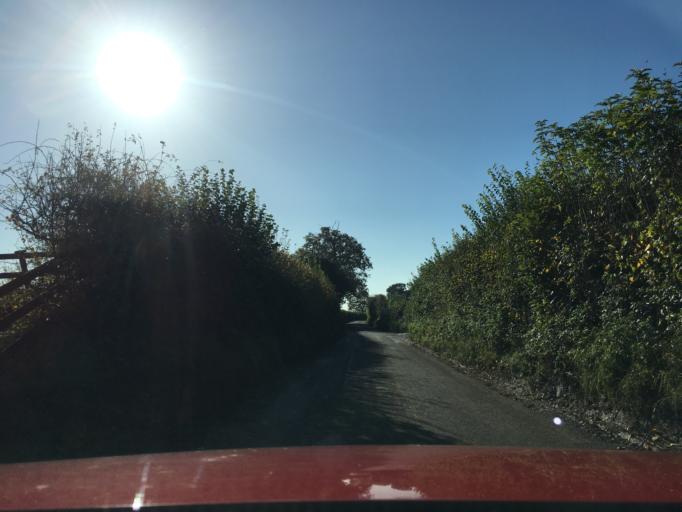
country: GB
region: England
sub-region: Somerset
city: Yeovil
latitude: 50.9164
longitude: -2.6183
